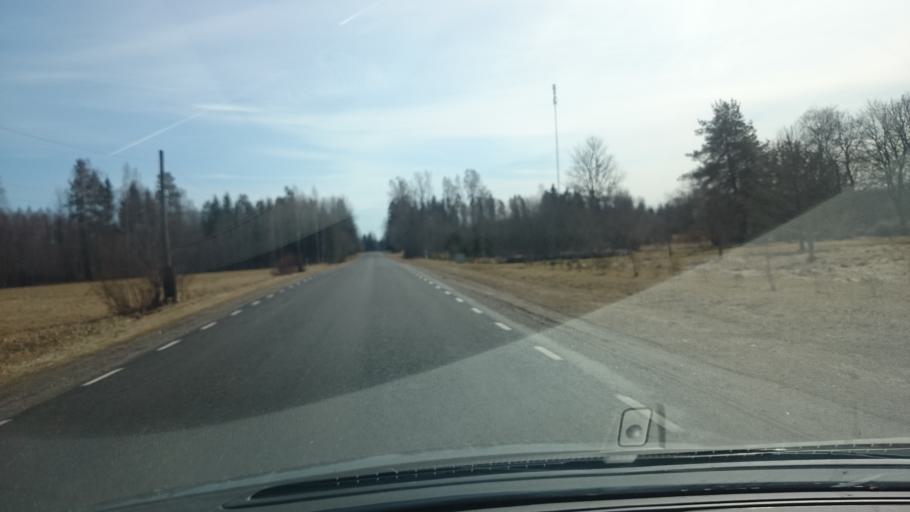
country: EE
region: Paernumaa
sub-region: Vaendra vald (alev)
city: Vandra
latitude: 58.6317
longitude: 24.9171
